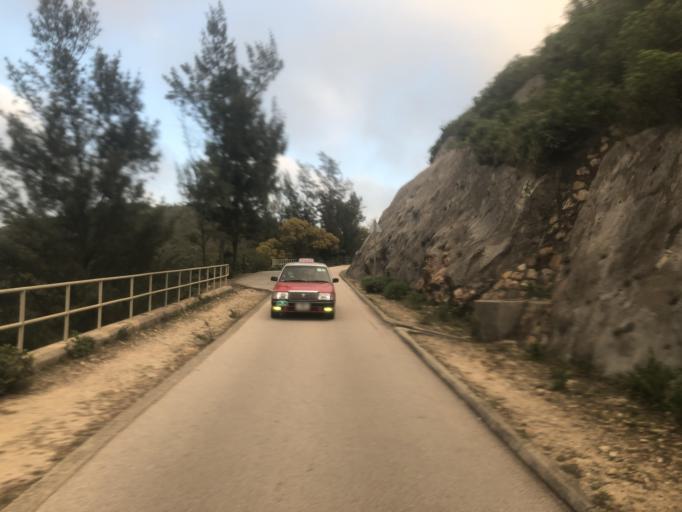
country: HK
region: Sai Kung
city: Sai Kung
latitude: 22.3639
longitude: 114.3491
